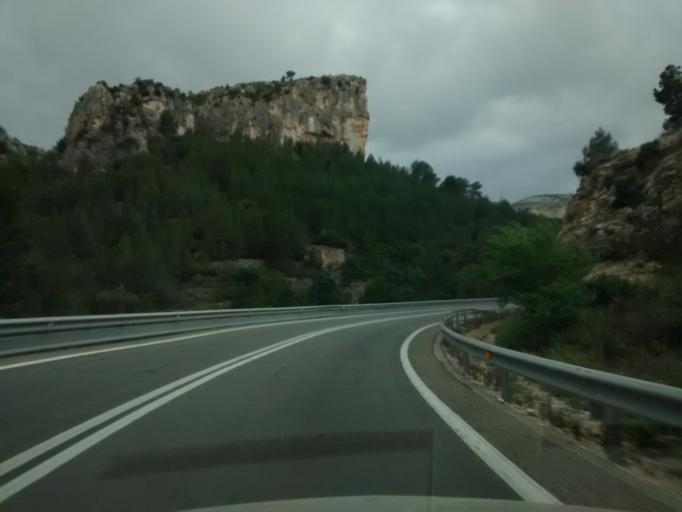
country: ES
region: Catalonia
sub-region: Provincia de Tarragona
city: Gandesa
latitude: 41.0383
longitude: 0.4888
